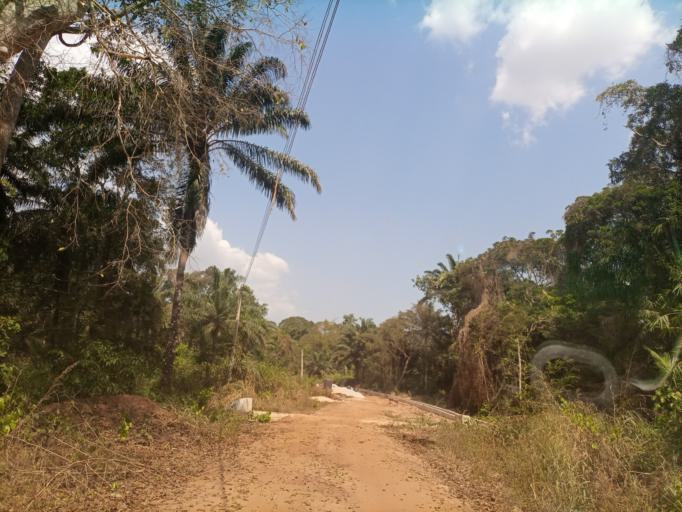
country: NG
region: Enugu
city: Obollo-Afor
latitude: 6.8823
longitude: 7.5190
